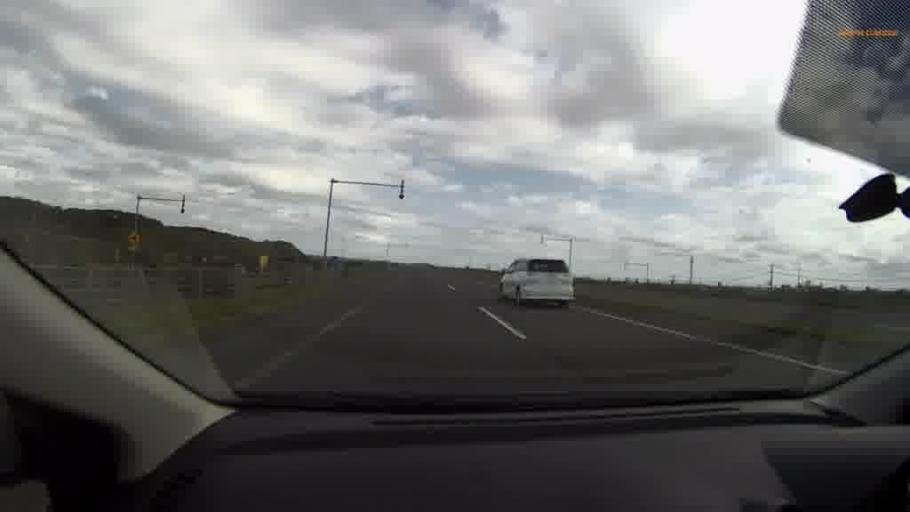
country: JP
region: Hokkaido
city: Kushiro
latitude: 43.0071
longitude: 144.2556
